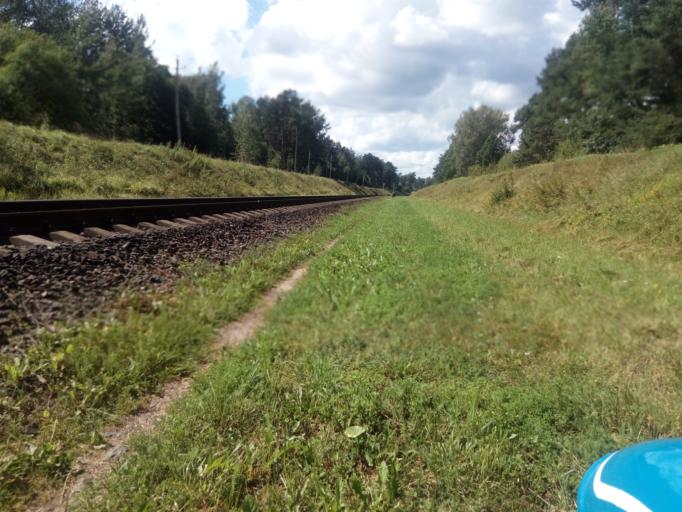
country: BY
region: Vitebsk
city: Dzisna
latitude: 55.6784
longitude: 28.2976
